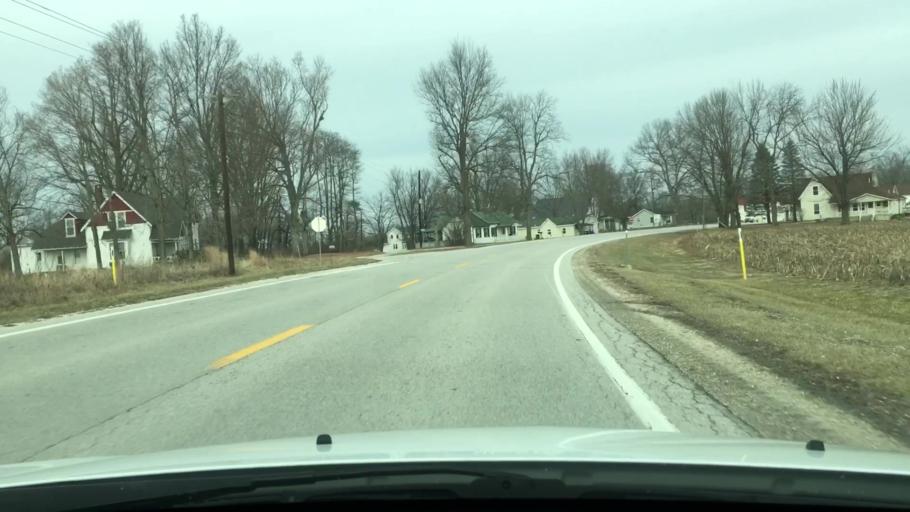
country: US
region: Illinois
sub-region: Pike County
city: Pittsfield
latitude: 39.5440
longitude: -90.9204
